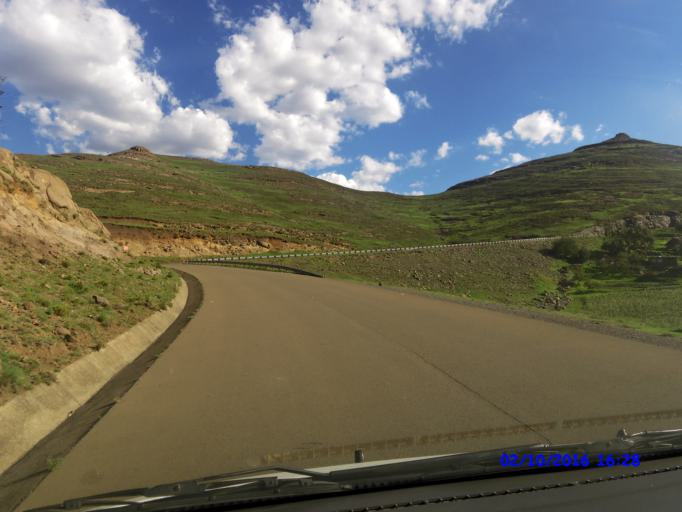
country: LS
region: Maseru
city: Nako
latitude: -29.4730
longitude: 28.0885
